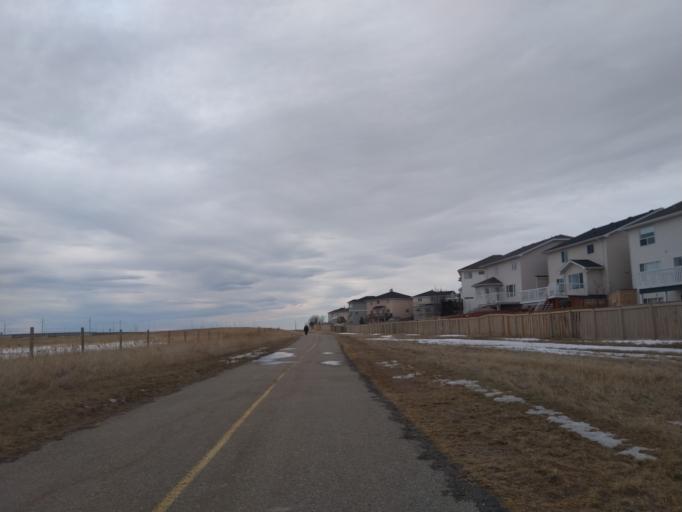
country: CA
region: Alberta
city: Chestermere
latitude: 51.1037
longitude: -113.9226
